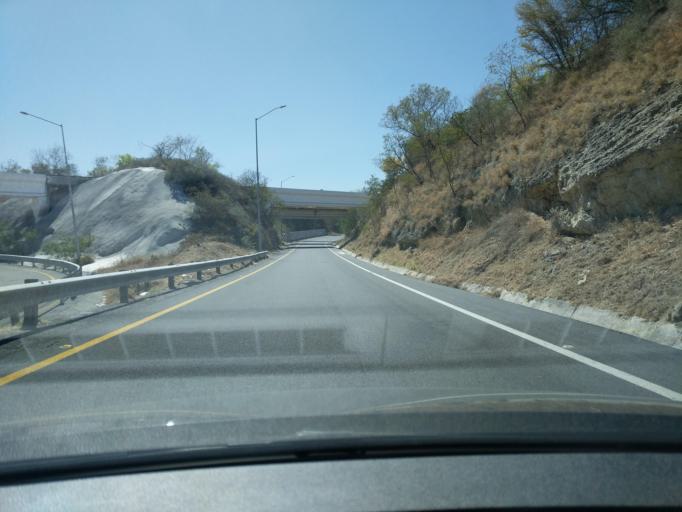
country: MX
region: Nuevo Leon
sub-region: Juarez
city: San Antonio
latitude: 25.6573
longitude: -100.0714
